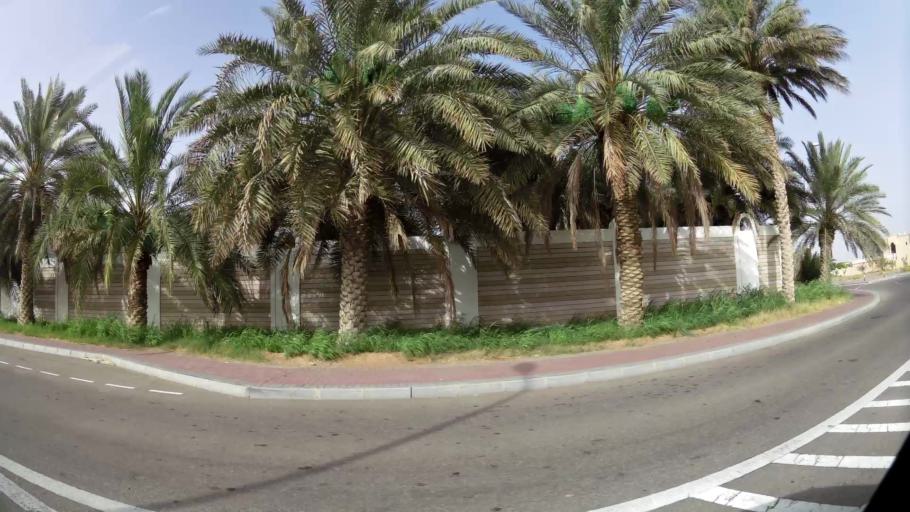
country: AE
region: Abu Dhabi
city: Al Ain
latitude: 24.1948
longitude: 55.6131
